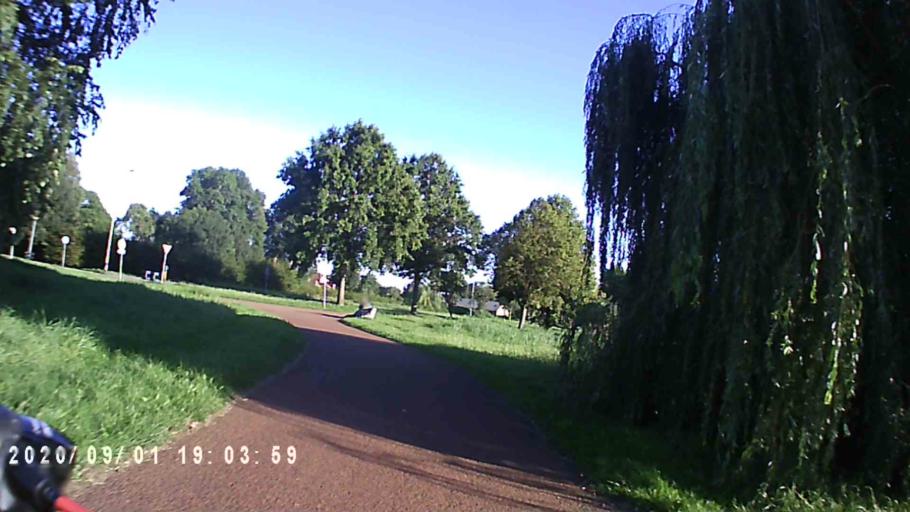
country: NL
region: Groningen
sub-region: Gemeente Veendam
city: Veendam
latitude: 53.1131
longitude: 6.8711
